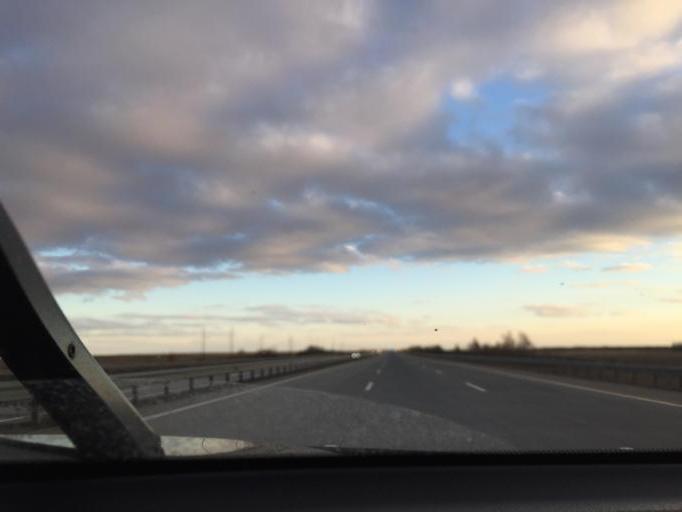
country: KZ
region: Astana Qalasy
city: Astana
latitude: 51.3501
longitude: 71.3367
